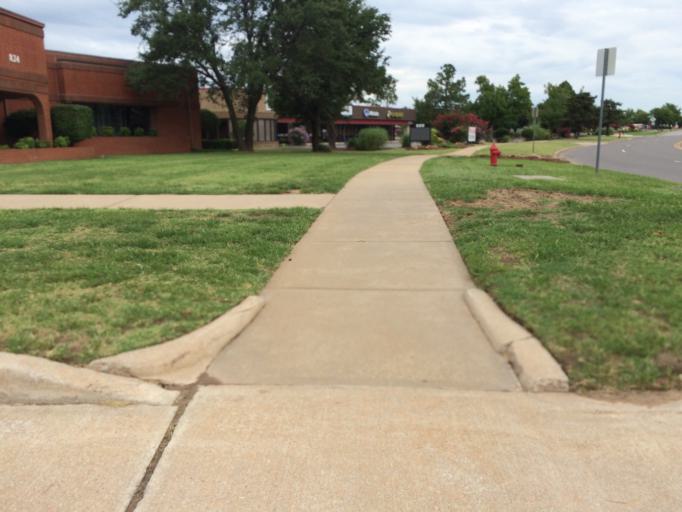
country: US
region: Oklahoma
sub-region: Cleveland County
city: Norman
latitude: 35.2290
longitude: -97.4804
